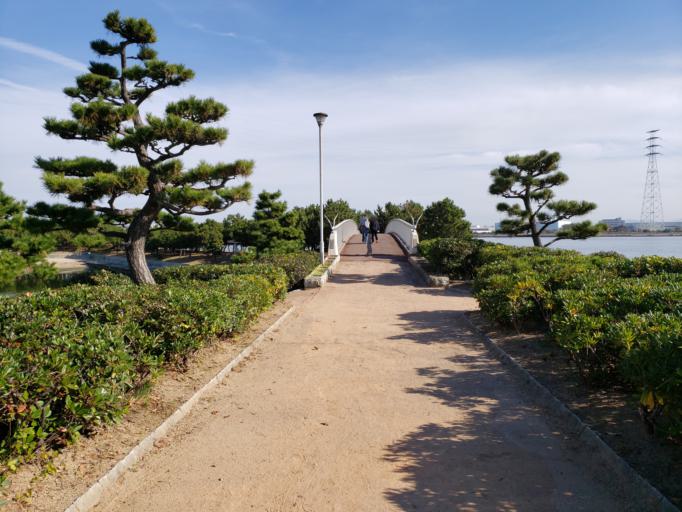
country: JP
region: Hyogo
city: Kakogawacho-honmachi
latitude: 34.7322
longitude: 134.8029
